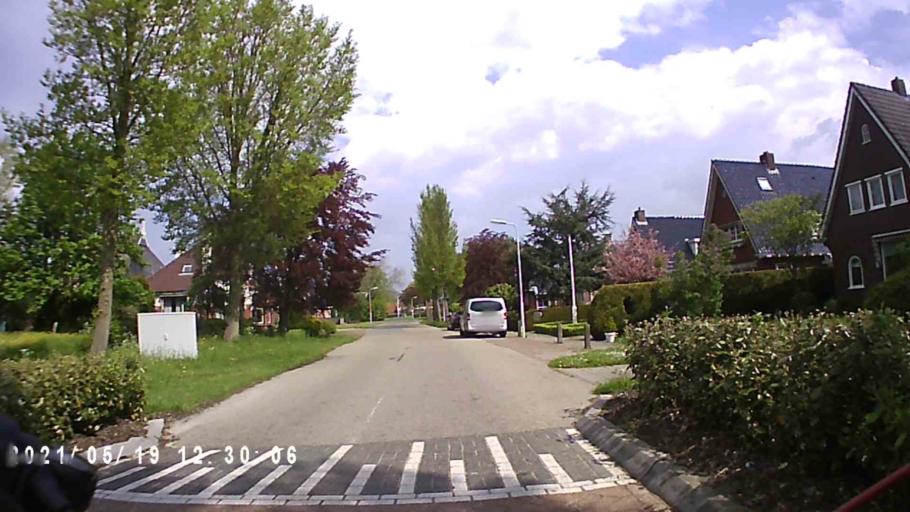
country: NL
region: Groningen
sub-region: Gemeente Grootegast
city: Grootegast
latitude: 53.2716
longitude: 6.2289
